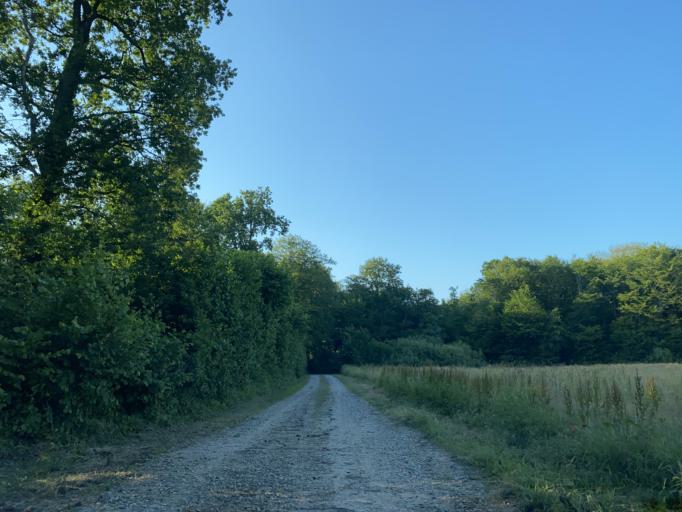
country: DK
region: South Denmark
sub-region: Haderslev Kommune
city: Starup
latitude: 55.1656
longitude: 9.5115
